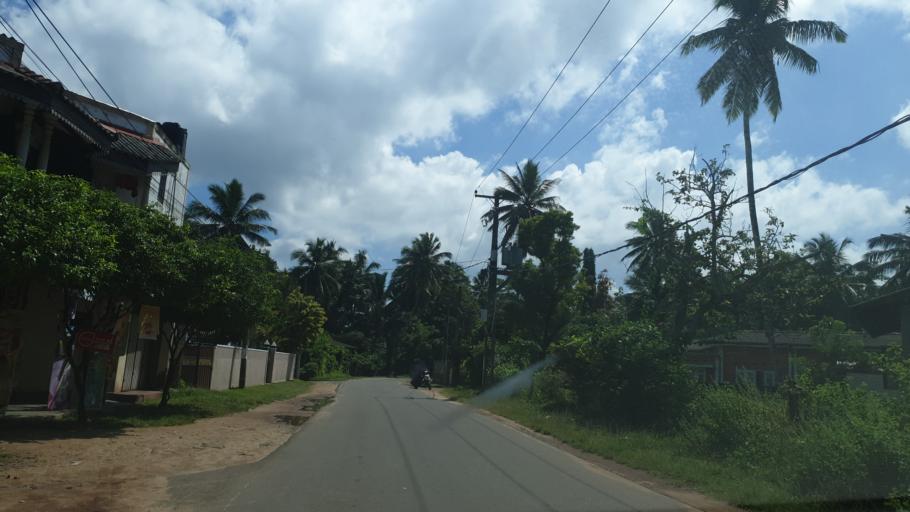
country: LK
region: Western
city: Panadura
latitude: 6.6759
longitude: 79.9309
